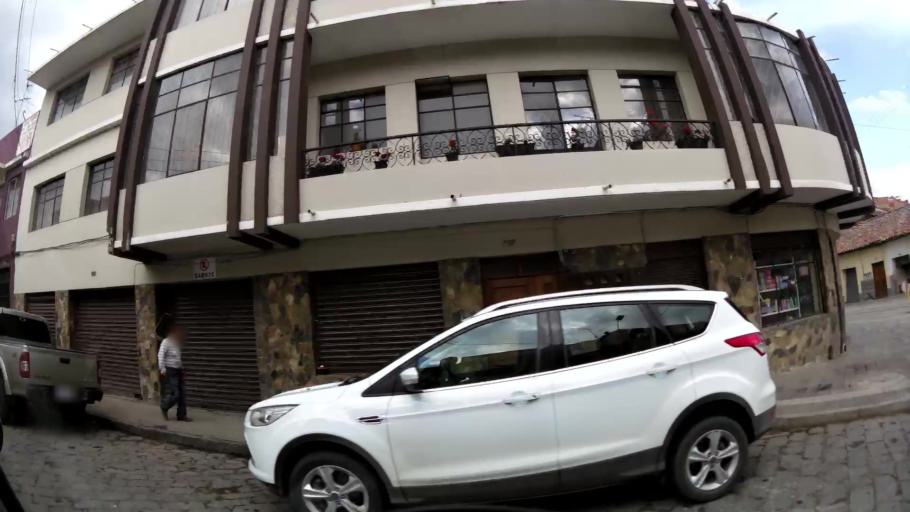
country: EC
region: Azuay
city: Cuenca
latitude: -2.8929
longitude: -79.0114
